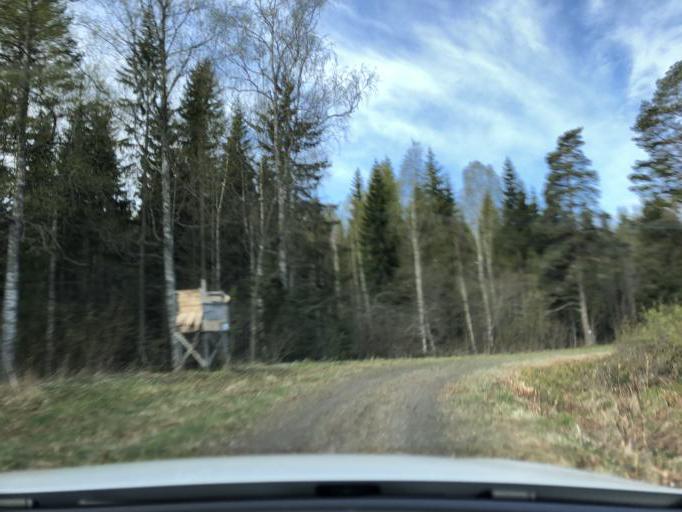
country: SE
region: Uppsala
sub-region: Heby Kommun
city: Tarnsjo
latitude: 60.2928
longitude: 16.8191
